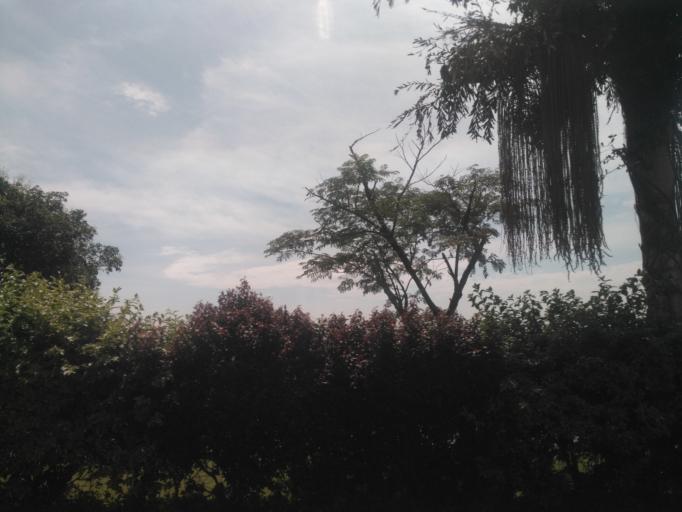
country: UG
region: Central Region
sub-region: Wakiso District
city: Entebbe
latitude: 0.0716
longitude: 32.4839
